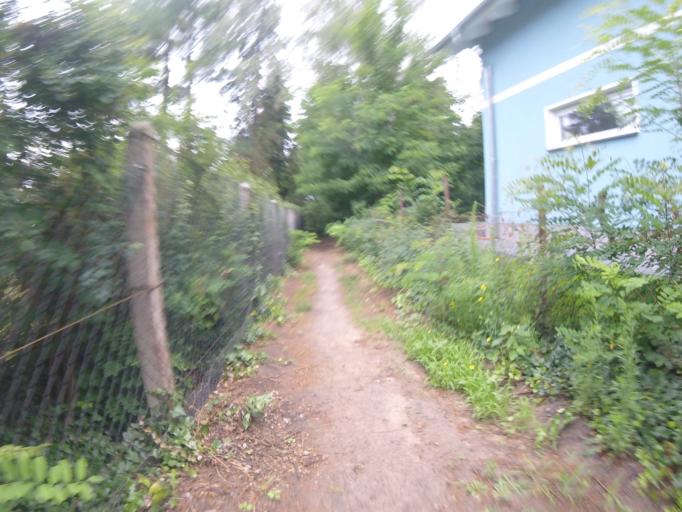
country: DE
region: Brandenburg
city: Bestensee
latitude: 52.2890
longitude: 13.6906
